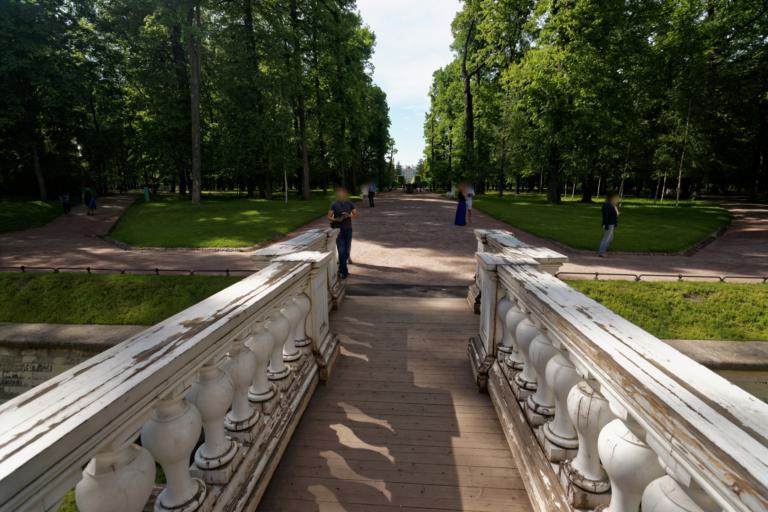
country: RU
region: St.-Petersburg
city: Pushkin
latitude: 59.7136
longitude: 30.4030
